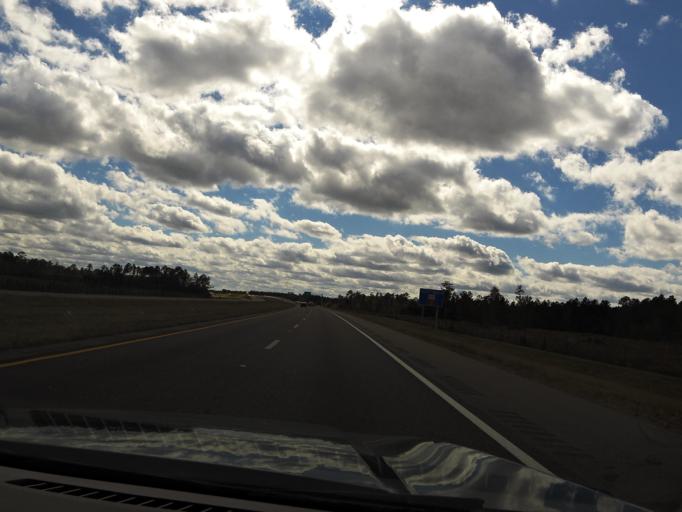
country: US
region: Florida
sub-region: Bradford County
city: Starke
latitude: 29.9532
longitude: -82.1373
